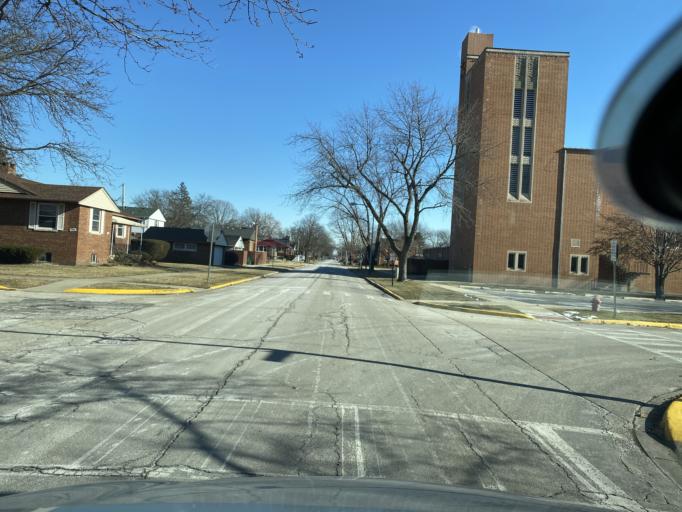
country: US
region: Illinois
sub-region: Cook County
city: Westchester
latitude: 41.8561
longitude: -87.8761
